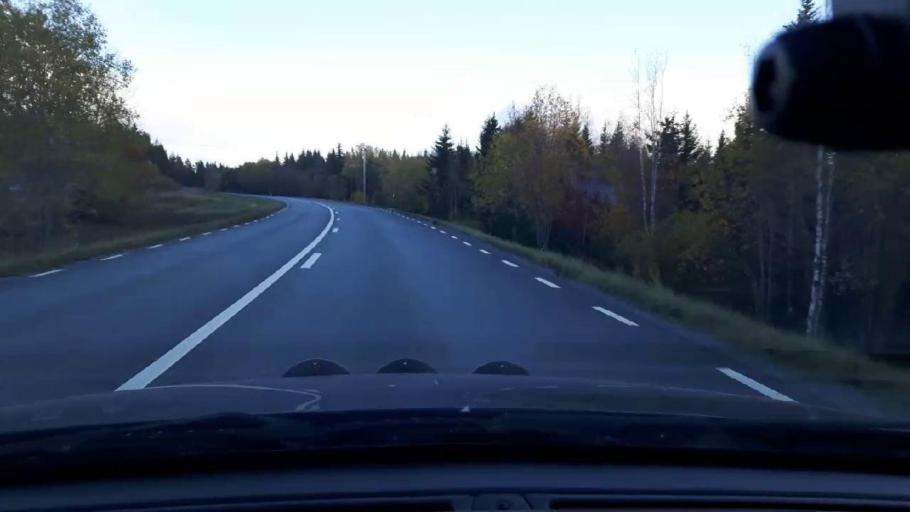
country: SE
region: Jaemtland
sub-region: Krokoms Kommun
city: Krokom
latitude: 63.0747
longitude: 14.2958
